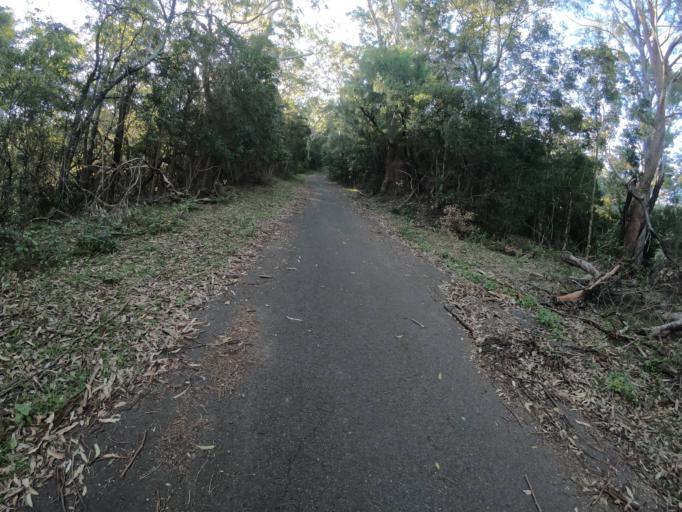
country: AU
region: New South Wales
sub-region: Wollongong
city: Mount Keira
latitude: -34.4124
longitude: 150.8357
